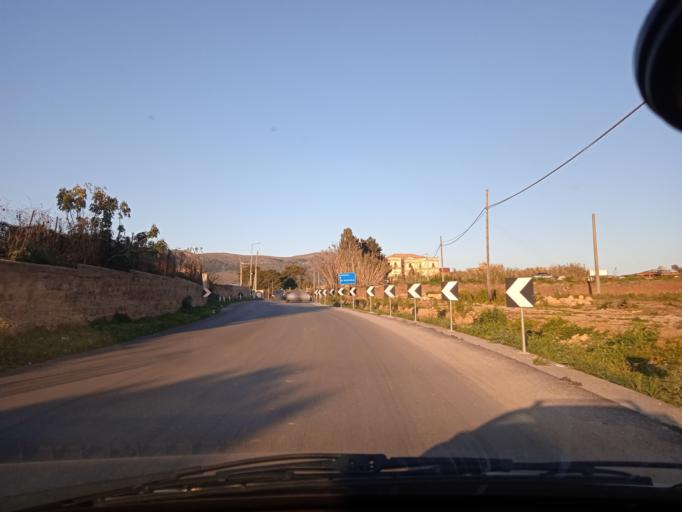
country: IT
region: Sicily
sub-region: Palermo
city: Bagheria
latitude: 38.0888
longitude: 13.4973
